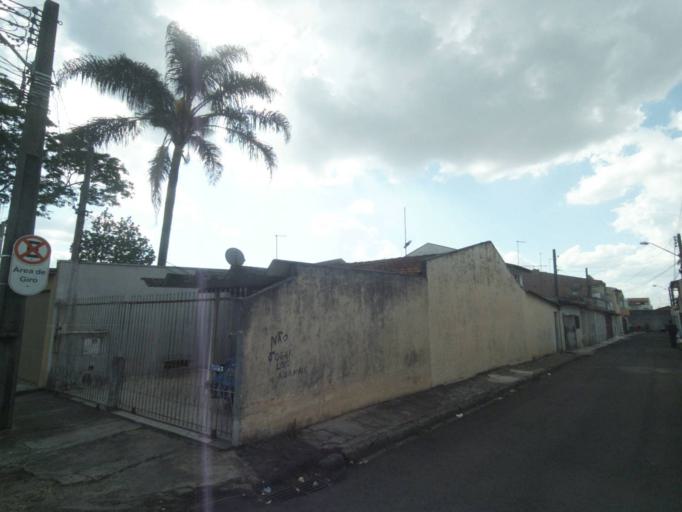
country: BR
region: Parana
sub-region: Sao Jose Dos Pinhais
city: Sao Jose dos Pinhais
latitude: -25.5318
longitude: -49.2630
